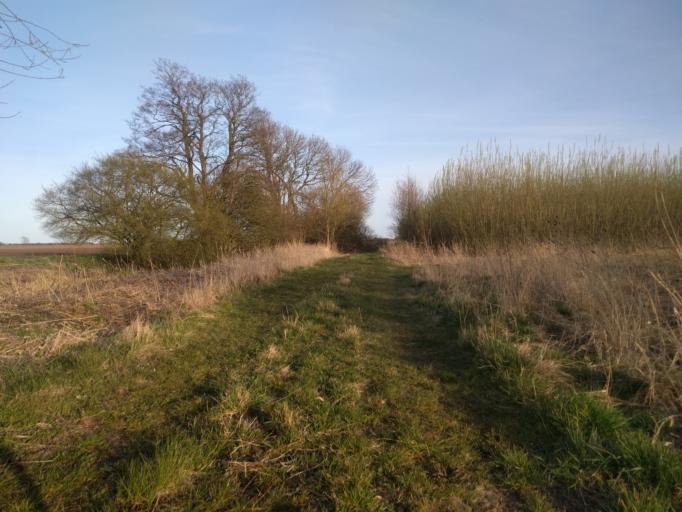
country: DK
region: South Denmark
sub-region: Kerteminde Kommune
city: Munkebo
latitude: 55.4120
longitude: 10.5501
